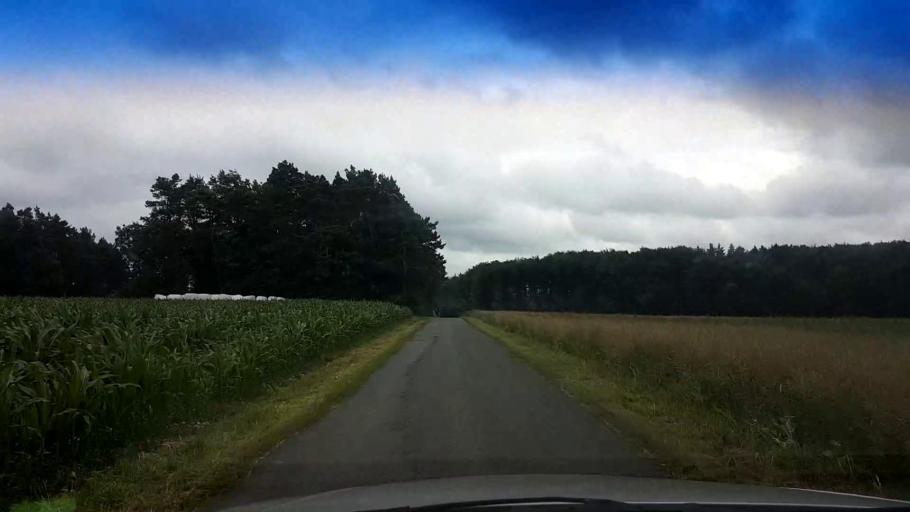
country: DE
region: Bavaria
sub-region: Upper Franconia
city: Poxdorf
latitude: 49.9013
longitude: 11.0811
